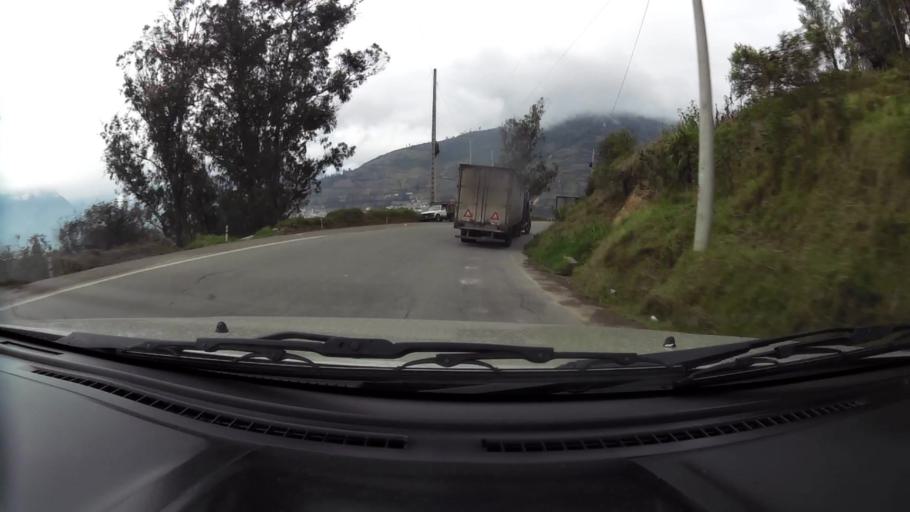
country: EC
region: Chimborazo
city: Alausi
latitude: -2.3064
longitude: -78.9204
